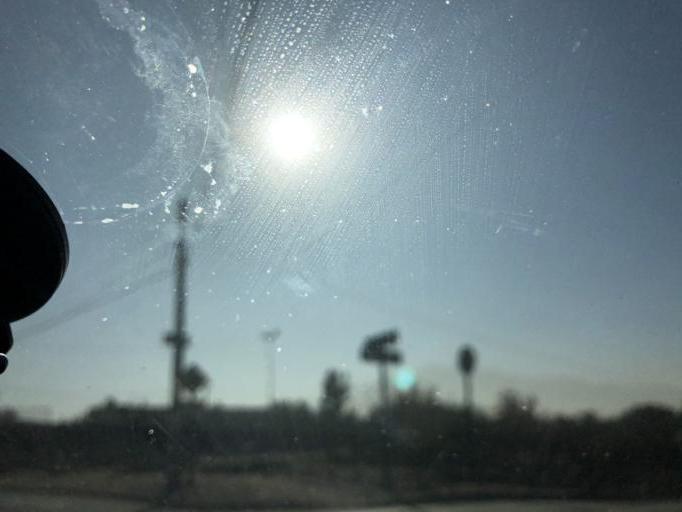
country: CL
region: Santiago Metropolitan
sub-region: Provincia de Cordillera
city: Puente Alto
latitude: -33.6252
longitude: -70.5918
